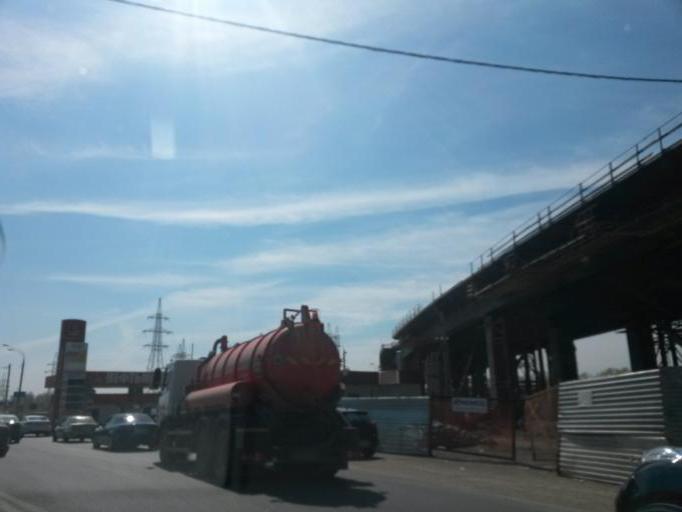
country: RU
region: Moskovskaya
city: Klimovsk
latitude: 55.3825
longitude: 37.5369
